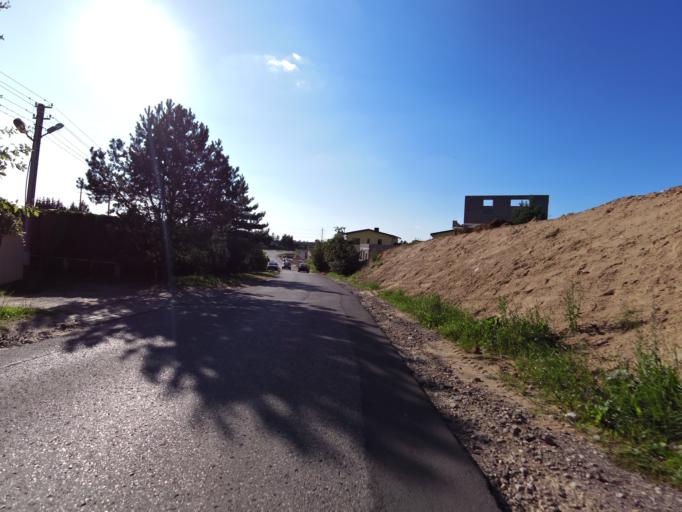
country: LT
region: Vilnius County
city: Pasilaiciai
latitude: 54.7311
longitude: 25.1882
